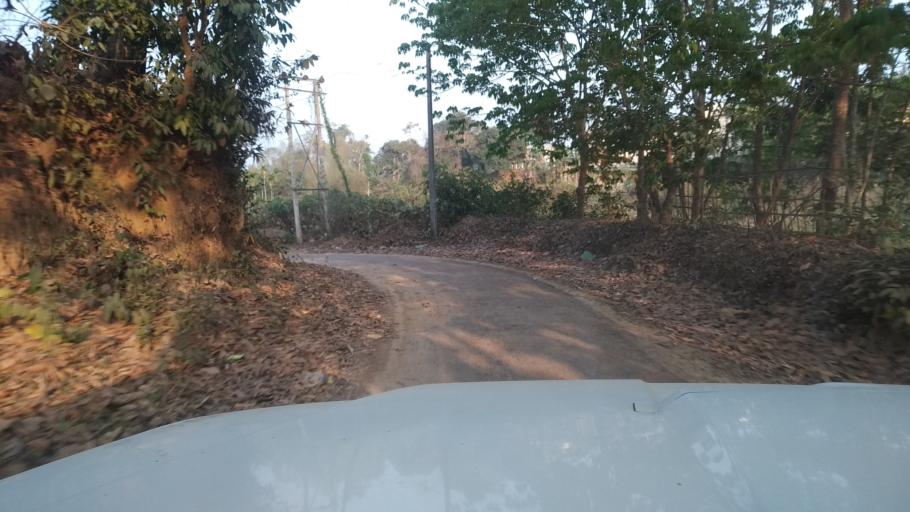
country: IN
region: Tripura
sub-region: South Tripura
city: Belonia
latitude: 23.3150
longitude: 91.3266
